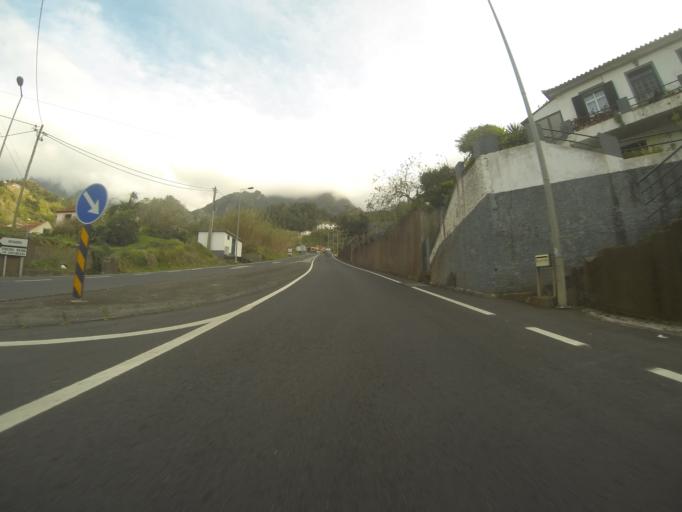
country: PT
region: Madeira
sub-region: Sao Vicente
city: Sao Vicente
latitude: 32.7758
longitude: -17.0329
